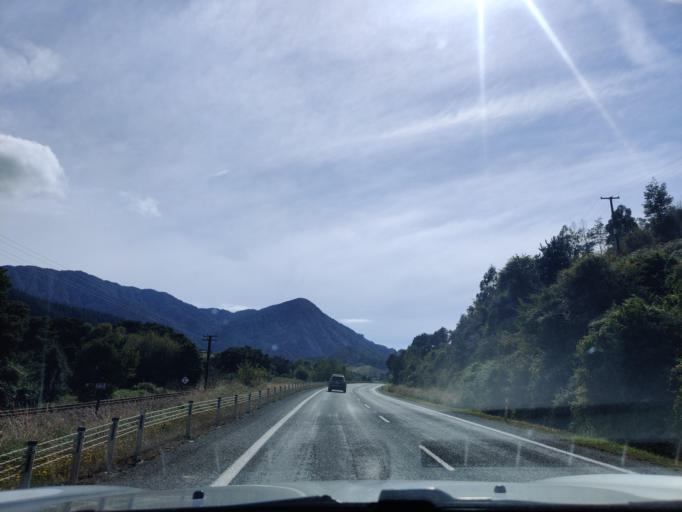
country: NZ
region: Marlborough
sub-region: Marlborough District
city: Picton
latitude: -41.3330
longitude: 173.9673
